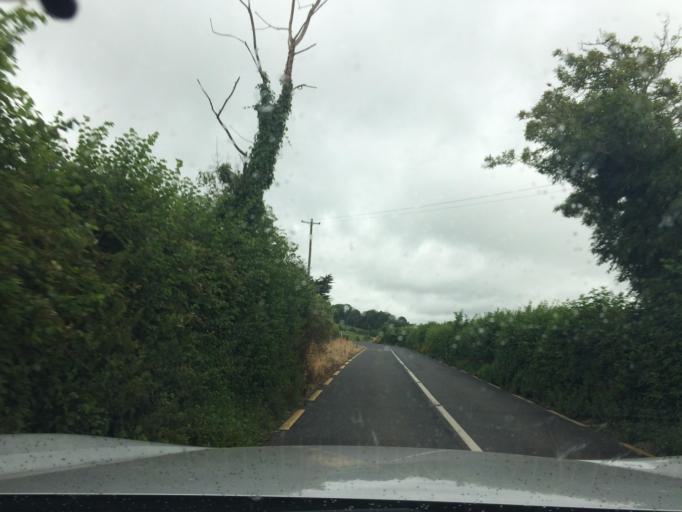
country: IE
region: Munster
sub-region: South Tipperary
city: Cluain Meala
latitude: 52.2917
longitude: -7.7677
